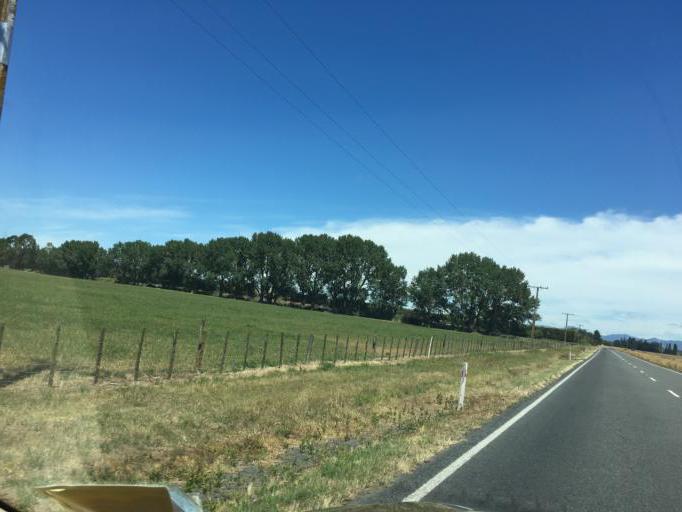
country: NZ
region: Hawke's Bay
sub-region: Hastings District
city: Hastings
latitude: -39.9968
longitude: 176.4183
